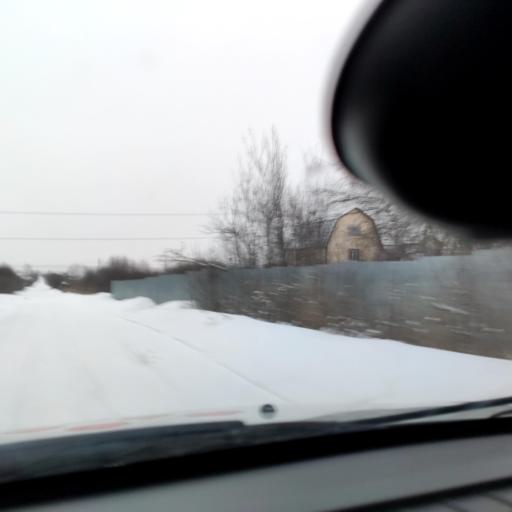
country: RU
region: Bashkortostan
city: Avdon
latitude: 54.5725
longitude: 55.7366
